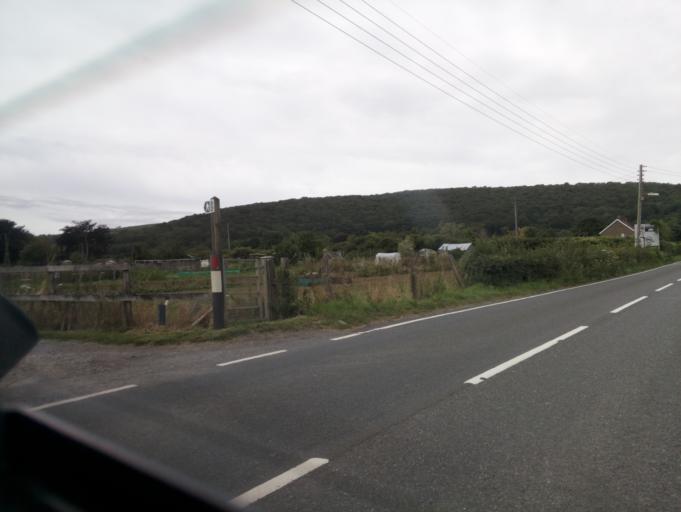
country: GB
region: England
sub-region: Somerset
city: Cheddar
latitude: 51.2859
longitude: -2.7901
